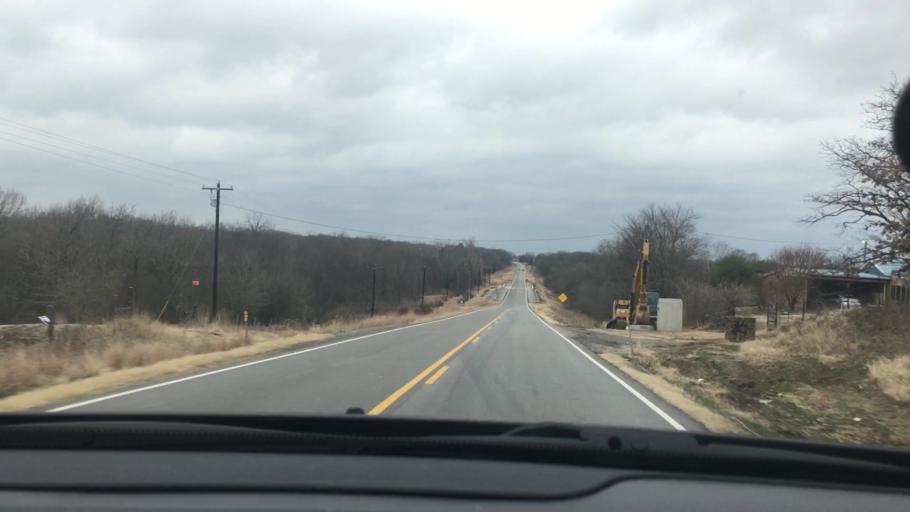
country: US
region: Oklahoma
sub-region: Atoka County
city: Atoka
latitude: 34.3791
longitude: -96.2748
